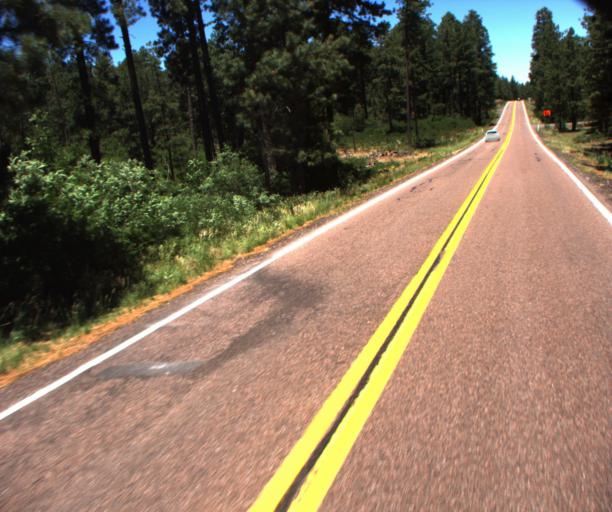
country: US
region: Arizona
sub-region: Gila County
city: Pine
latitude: 34.4773
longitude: -111.3812
